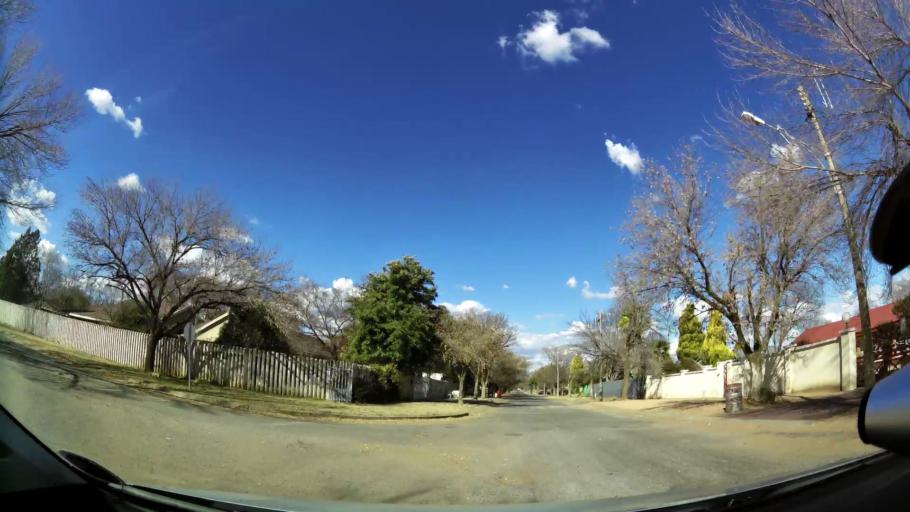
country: ZA
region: North-West
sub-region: Dr Kenneth Kaunda District Municipality
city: Klerksdorp
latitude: -26.8421
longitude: 26.6485
